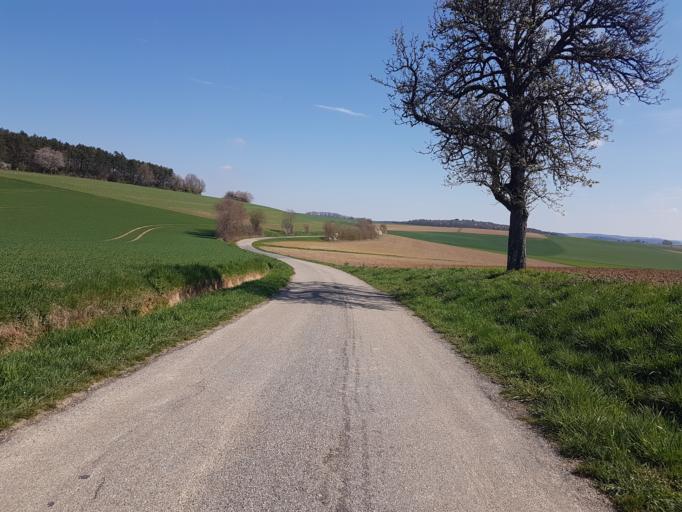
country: DE
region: Baden-Wuerttemberg
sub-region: Regierungsbezirk Stuttgart
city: Jagsthausen
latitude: 49.3576
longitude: 9.4887
